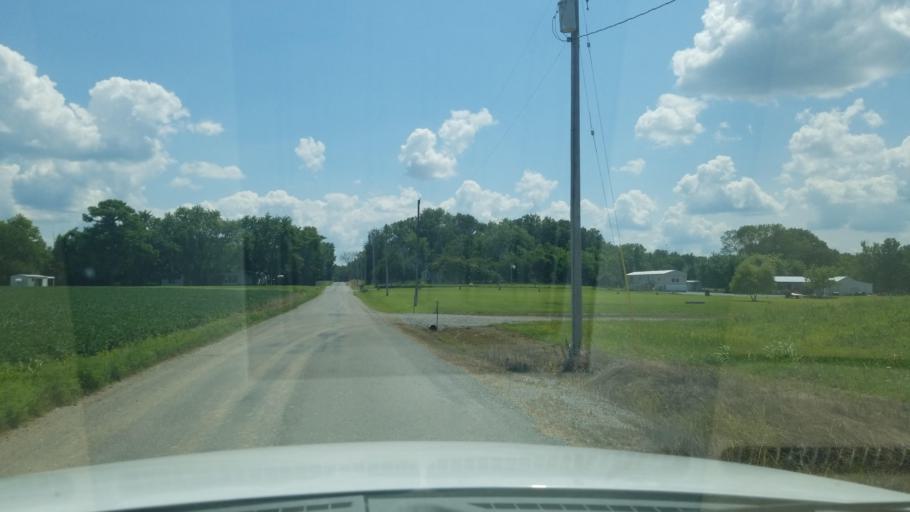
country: US
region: Illinois
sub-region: Saline County
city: Harrisburg
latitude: 37.7711
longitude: -88.5170
